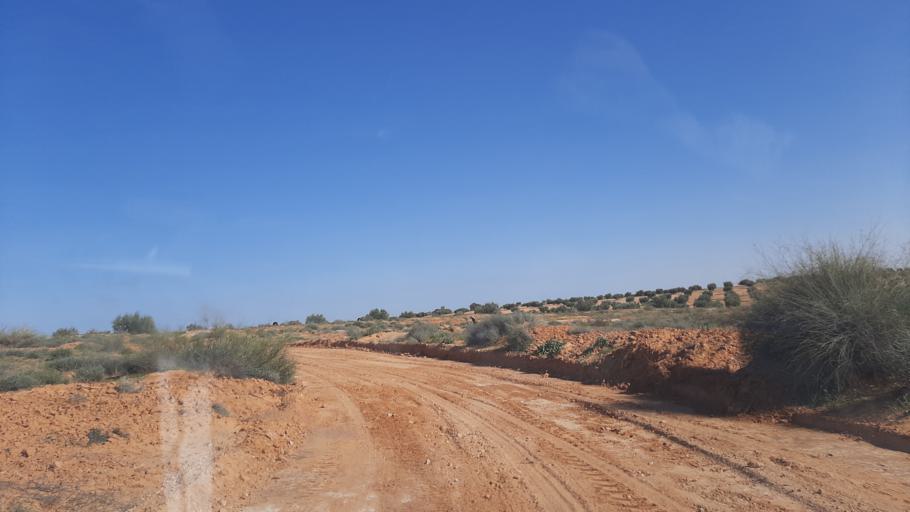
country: TN
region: Madanin
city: Medenine
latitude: 33.2814
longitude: 10.7822
